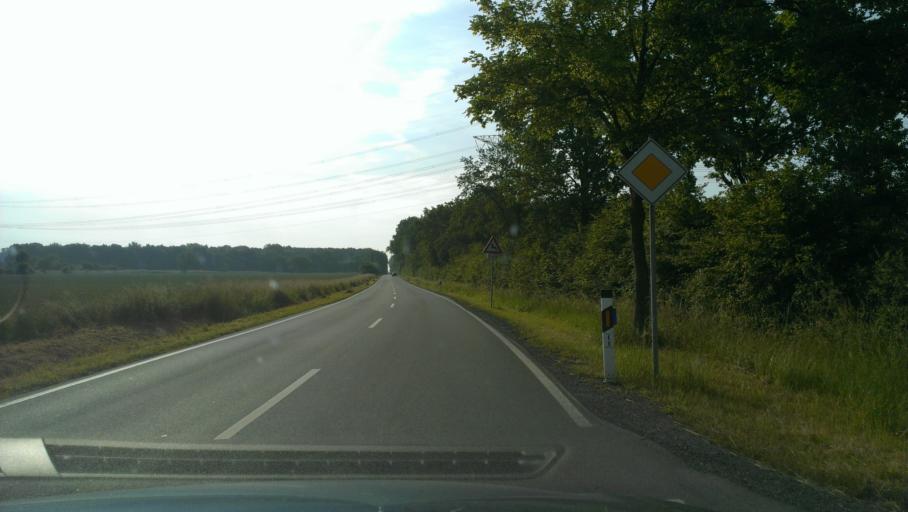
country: DE
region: North Rhine-Westphalia
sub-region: Regierungsbezirk Munster
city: Ennigerloh
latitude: 51.8138
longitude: 7.9724
